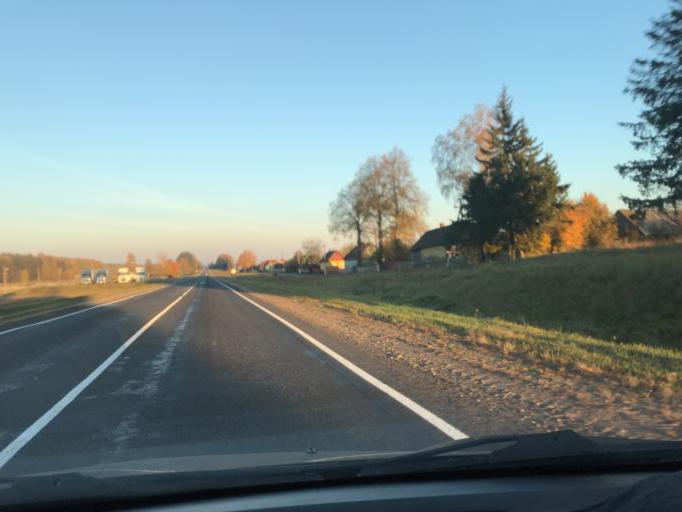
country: BY
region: Minsk
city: Staryya Darohi
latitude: 53.0596
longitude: 28.4748
